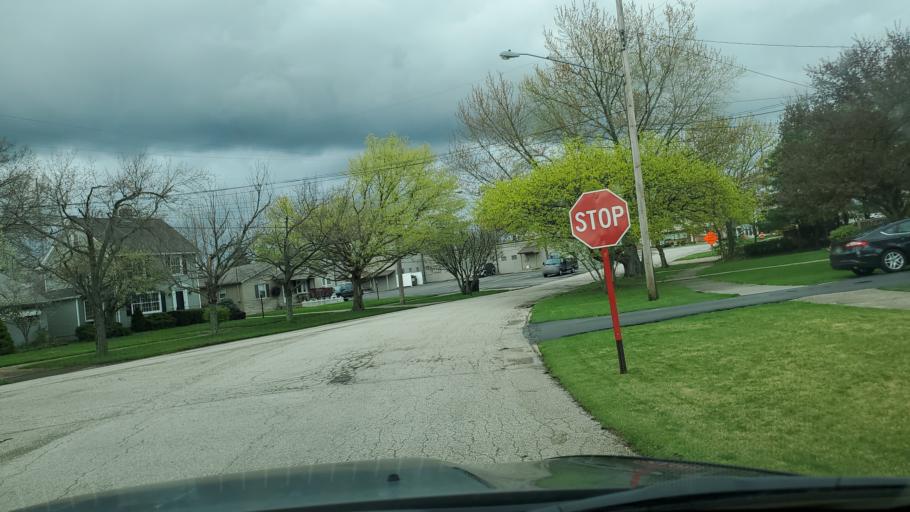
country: US
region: Ohio
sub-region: Mahoning County
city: Boardman
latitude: 41.0325
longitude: -80.6643
